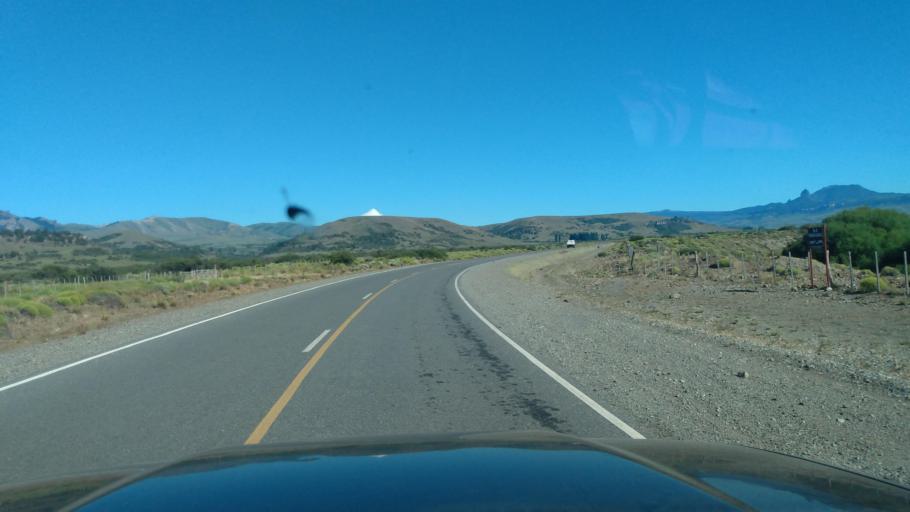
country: AR
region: Neuquen
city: Junin de los Andes
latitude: -39.8729
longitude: -71.1742
